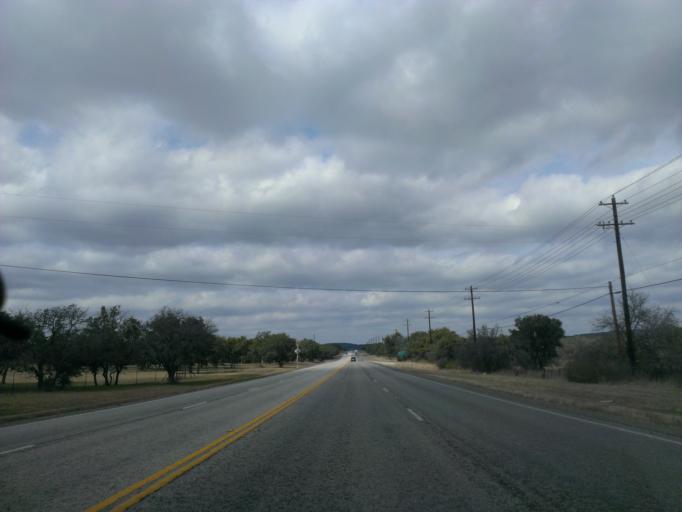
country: US
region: Texas
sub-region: Travis County
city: Briarcliff
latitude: 30.4104
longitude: -98.1100
